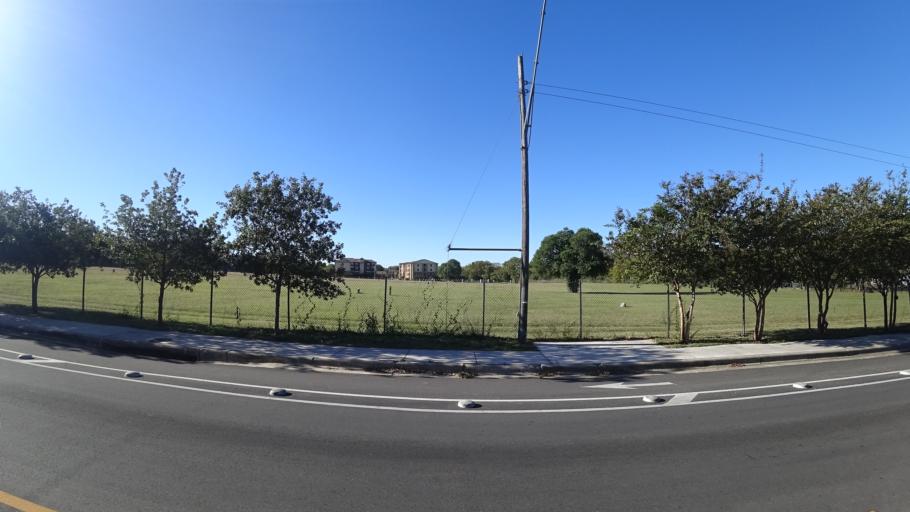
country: US
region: Texas
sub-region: Travis County
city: Austin
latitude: 30.3182
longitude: -97.7233
